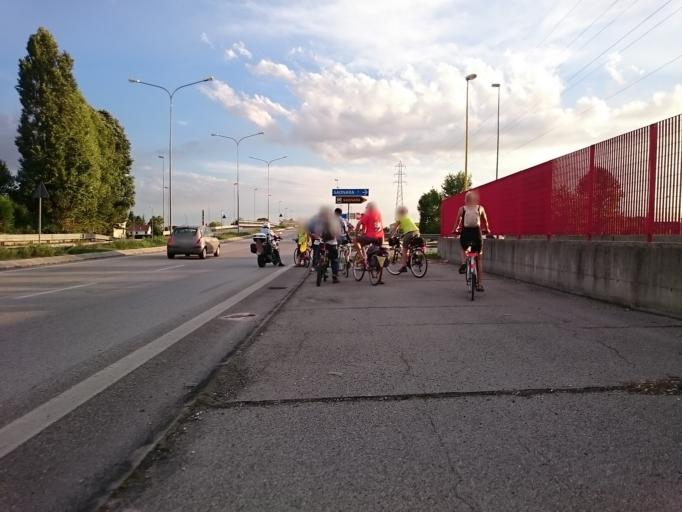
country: IT
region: Veneto
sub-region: Provincia di Padova
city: Ponte San Nicolo
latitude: 45.3836
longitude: 11.9399
